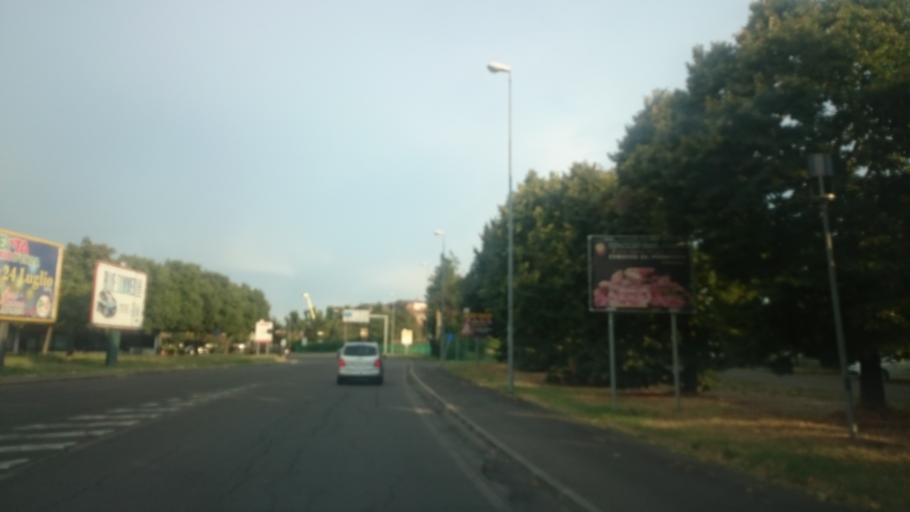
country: IT
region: Emilia-Romagna
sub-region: Provincia di Reggio Emilia
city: Reggio nell'Emilia
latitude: 44.7089
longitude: 10.6368
